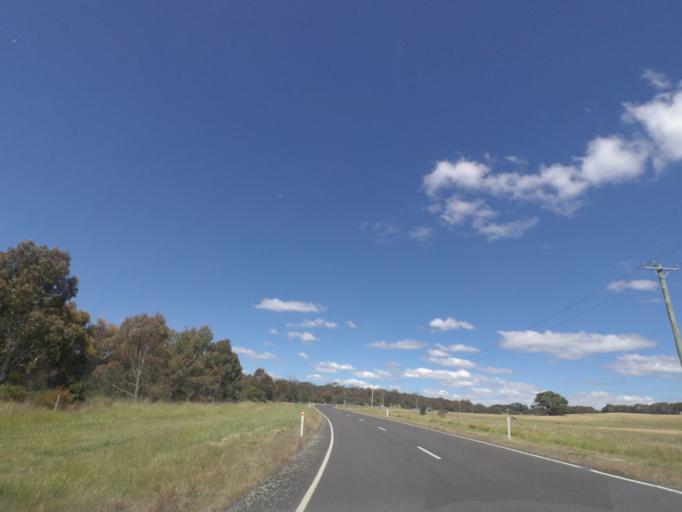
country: AU
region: Victoria
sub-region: Hume
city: Sunbury
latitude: -37.2972
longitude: 144.5019
